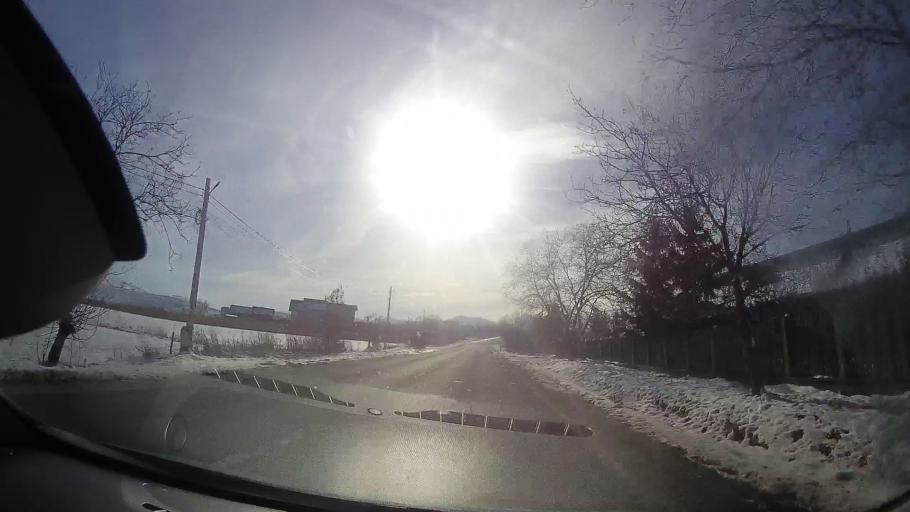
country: RO
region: Neamt
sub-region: Comuna Baltatesti
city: Valea Seaca
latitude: 47.1415
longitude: 26.3182
